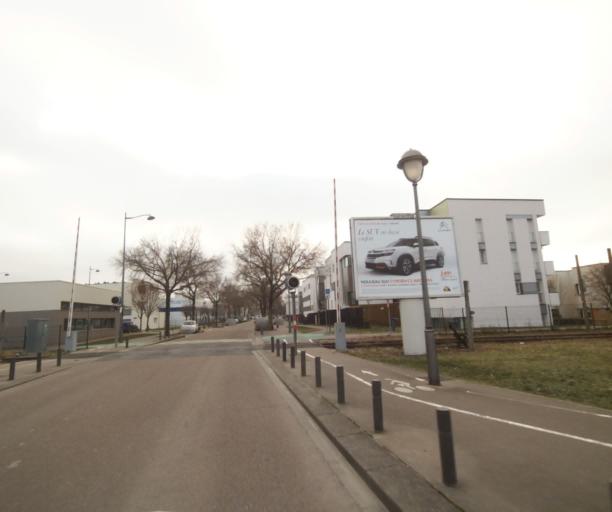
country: FR
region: Champagne-Ardenne
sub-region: Departement de la Haute-Marne
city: Bettancourt-la-Ferree
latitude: 48.6457
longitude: 4.9609
